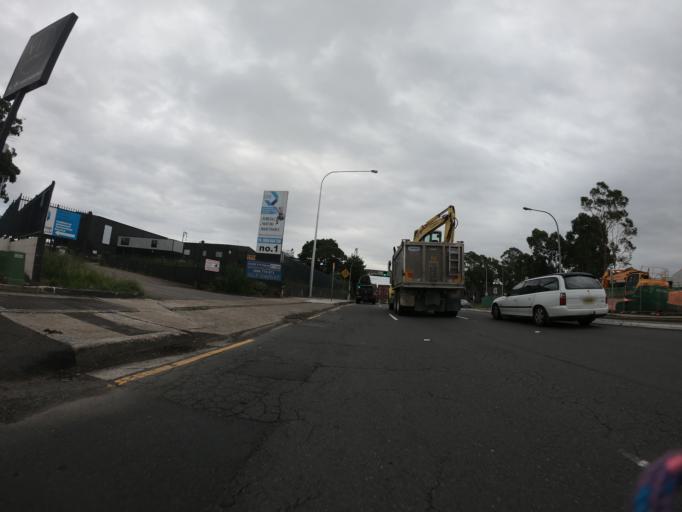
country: AU
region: New South Wales
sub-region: Parramatta
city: Harris Park
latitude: -33.8283
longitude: 151.0048
